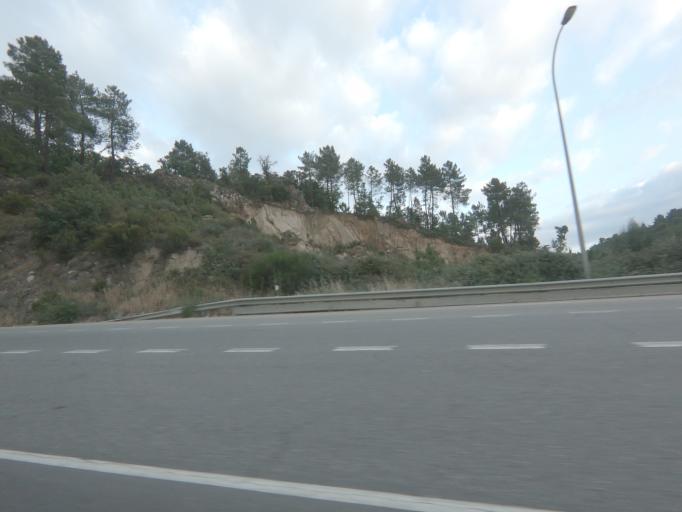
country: ES
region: Galicia
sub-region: Provincia de Ourense
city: Taboadela
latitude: 42.2816
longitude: -7.8497
